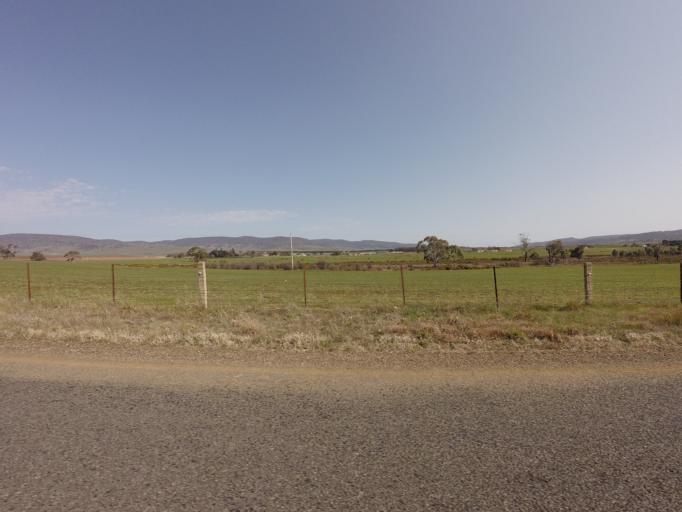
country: AU
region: Tasmania
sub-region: Northern Midlands
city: Evandale
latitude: -41.7933
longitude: 147.7442
